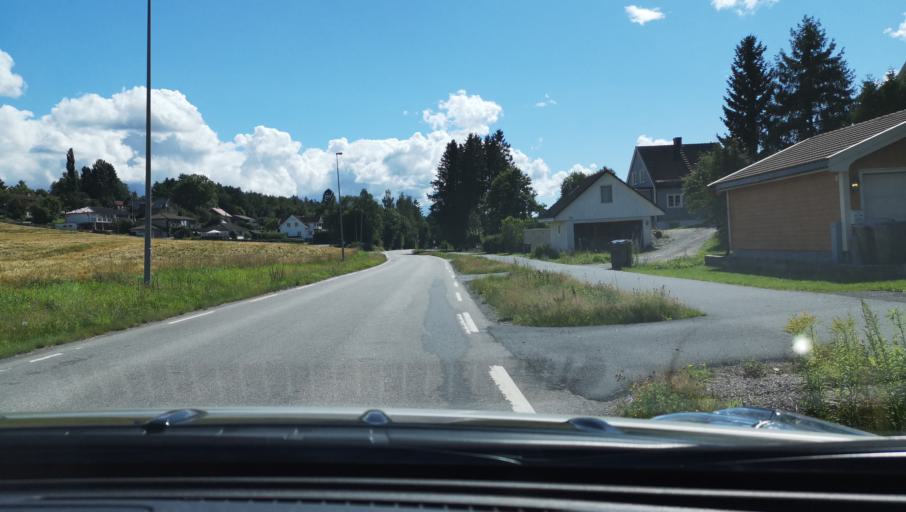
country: NO
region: Akershus
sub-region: As
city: As
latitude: 59.6566
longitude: 10.7993
